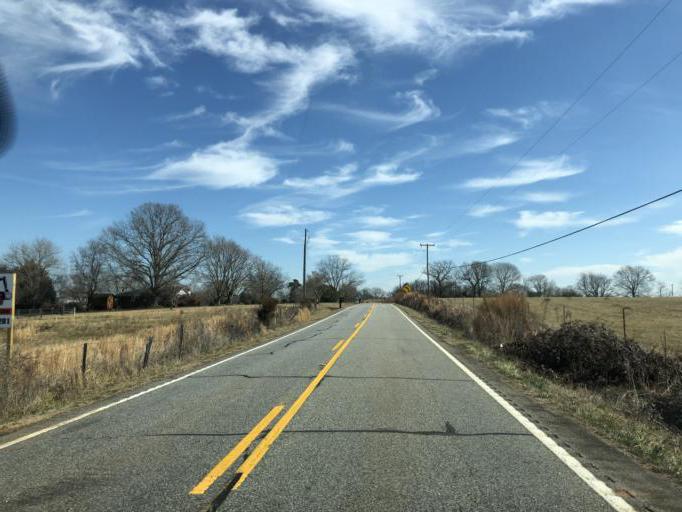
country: US
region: South Carolina
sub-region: Spartanburg County
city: Mayo
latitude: 35.0517
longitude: -81.9125
